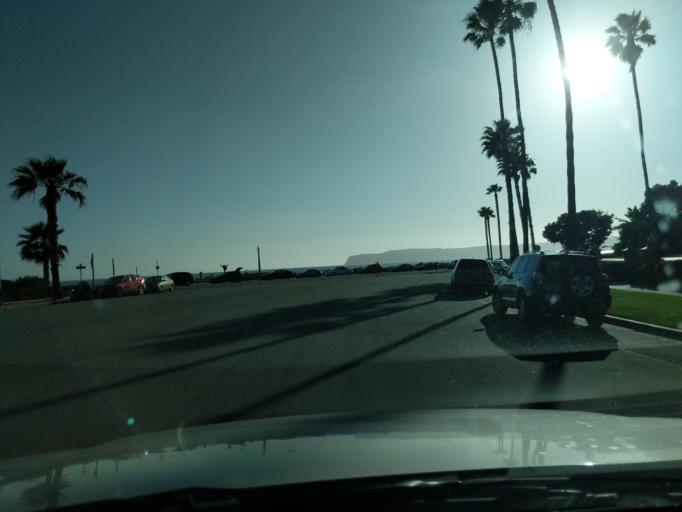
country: US
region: California
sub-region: San Diego County
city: Coronado
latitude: 32.6844
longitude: -117.1835
